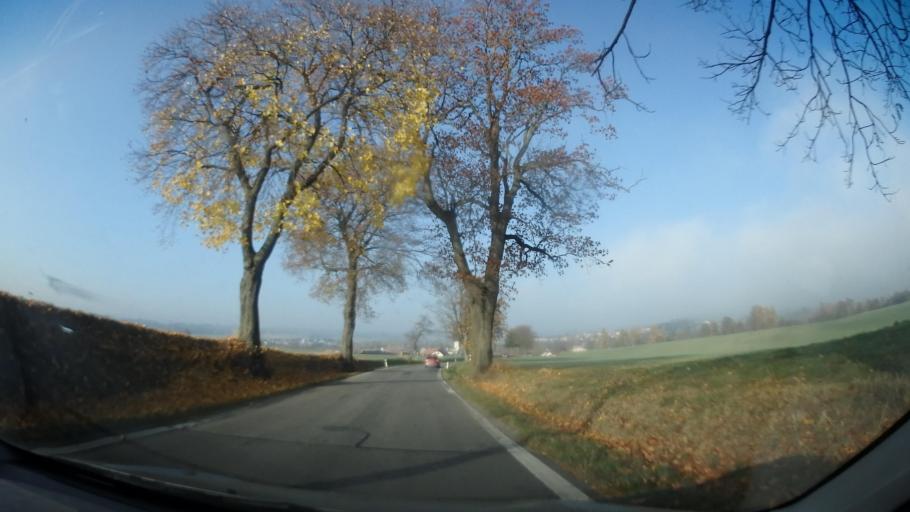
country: CZ
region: Vysocina
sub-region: Okres Zd'ar nad Sazavou
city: Nove Veseli
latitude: 49.4864
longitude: 15.9998
